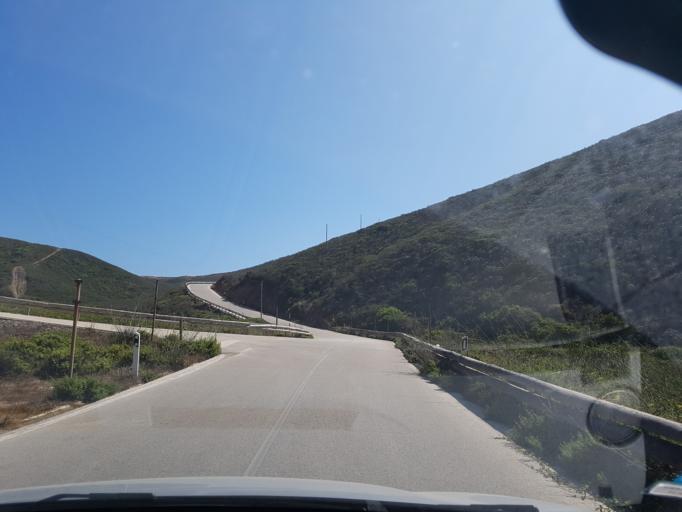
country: PT
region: Faro
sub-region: Vila do Bispo
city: Vila do Bispo
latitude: 37.1051
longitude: -8.9334
